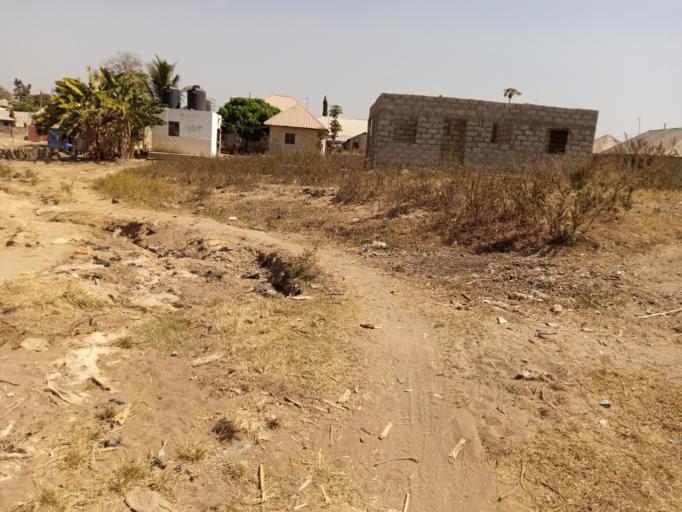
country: NG
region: Abuja Federal Capital Territory
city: Kuje
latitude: 8.9027
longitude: 7.3409
